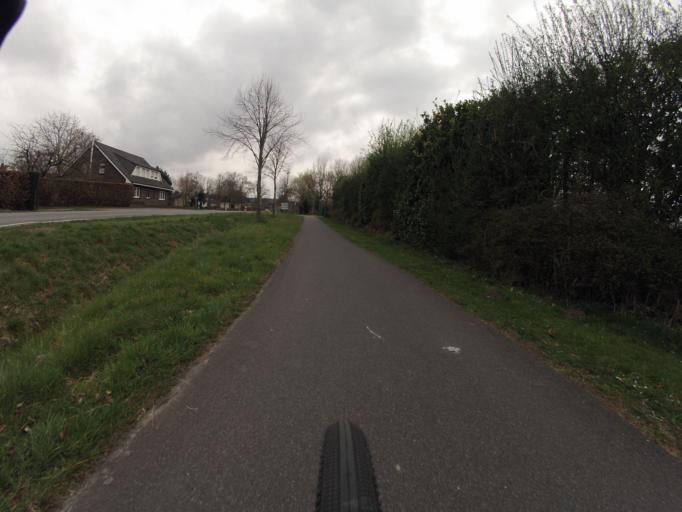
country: DE
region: North Rhine-Westphalia
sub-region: Regierungsbezirk Munster
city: Recke
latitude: 52.3513
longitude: 7.7147
